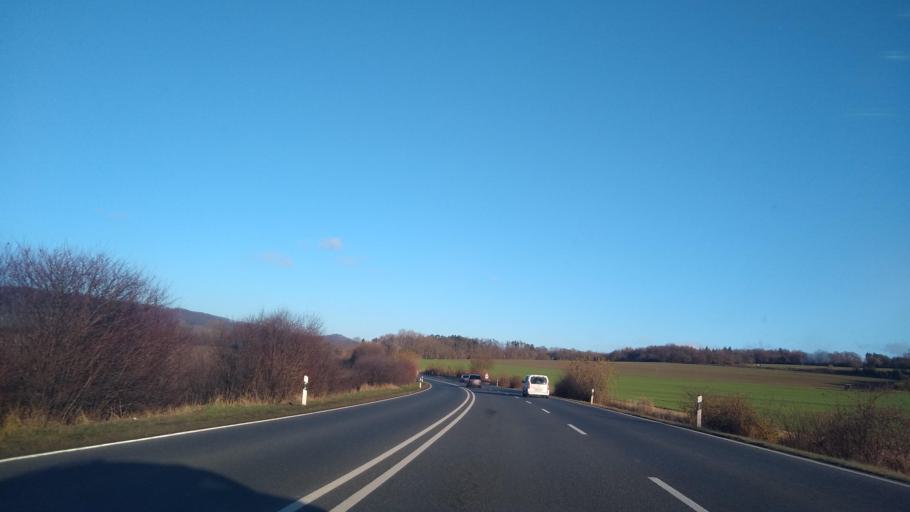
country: DE
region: Lower Saxony
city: Bevern
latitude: 51.8394
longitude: 9.4852
